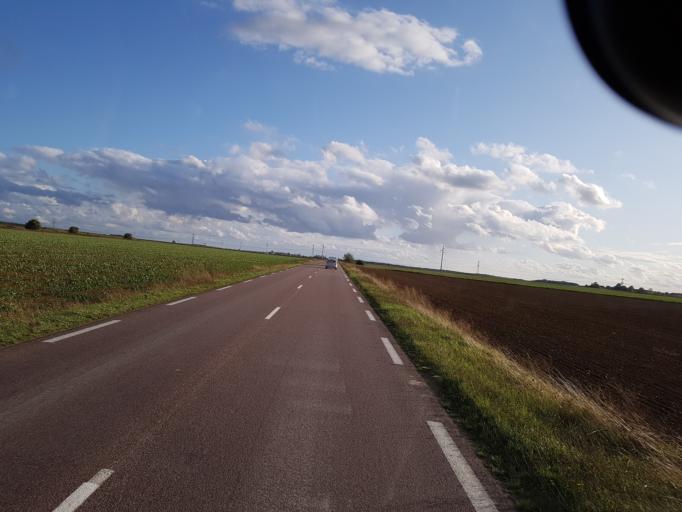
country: FR
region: Ile-de-France
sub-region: Departement de Seine-et-Marne
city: Jouy-le-Chatel
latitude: 48.6203
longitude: 3.1023
